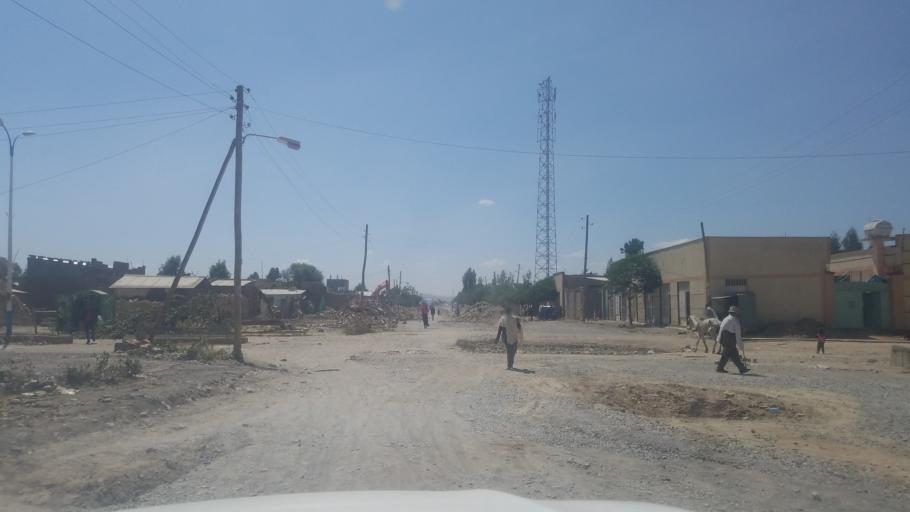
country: ET
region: Tigray
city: Mekele
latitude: 13.7897
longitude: 39.5983
